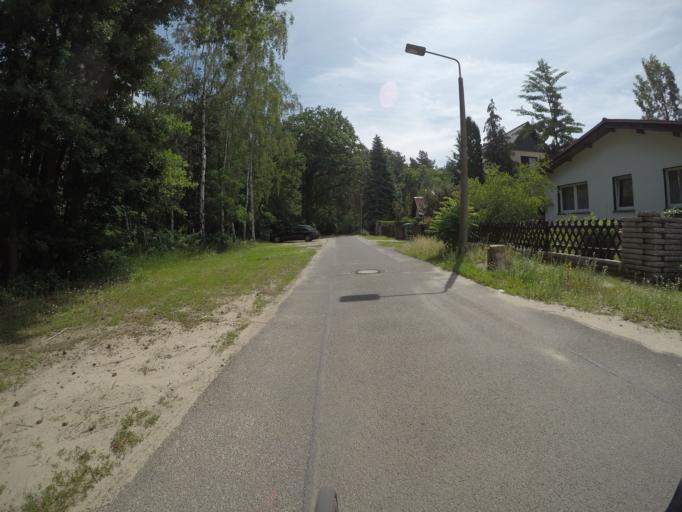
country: DE
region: Berlin
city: Berlin Koepenick
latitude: 52.4658
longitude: 13.5962
